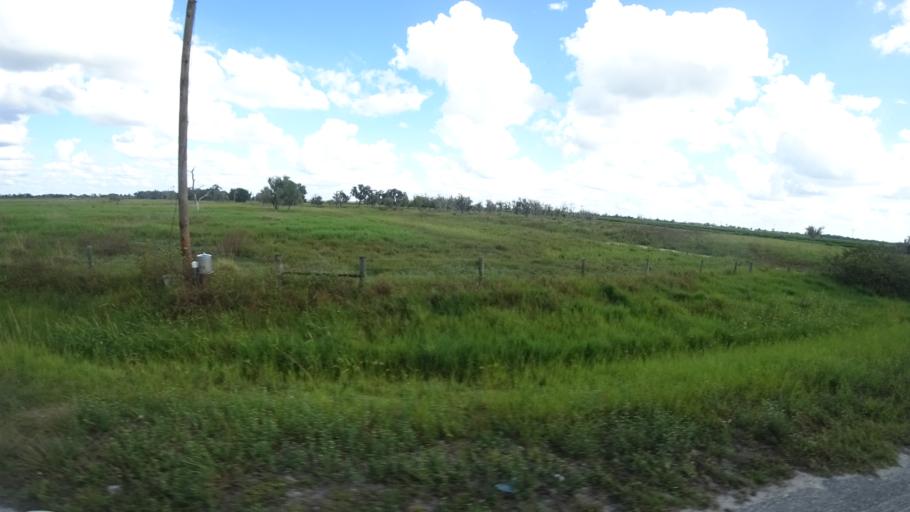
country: US
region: Florida
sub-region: DeSoto County
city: Nocatee
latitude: 27.2839
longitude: -82.1135
